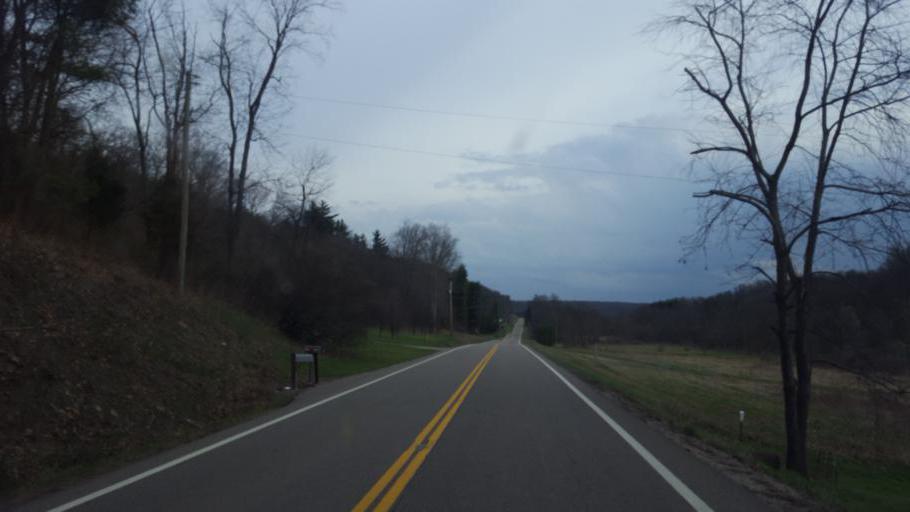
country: US
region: Ohio
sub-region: Guernsey County
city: Mantua
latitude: 40.1301
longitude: -81.7813
